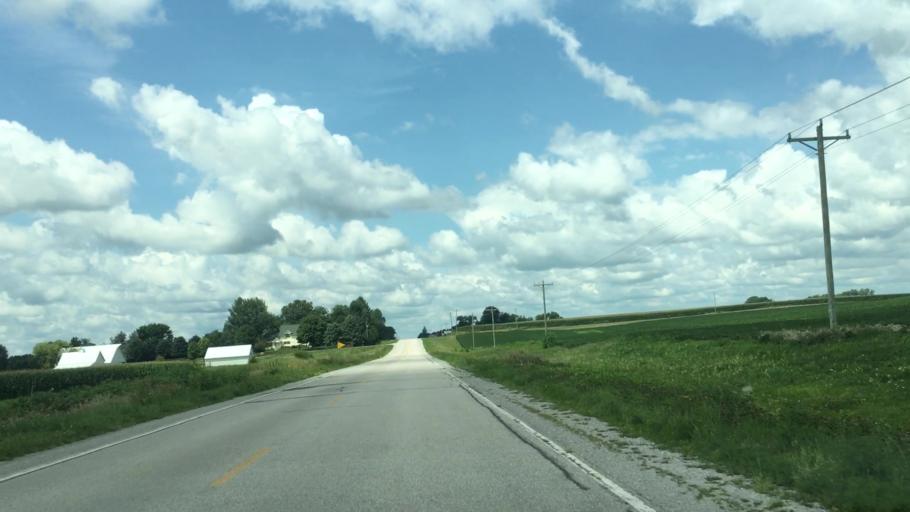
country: US
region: Iowa
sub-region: Johnson County
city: Solon
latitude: 41.8310
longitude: -91.4499
